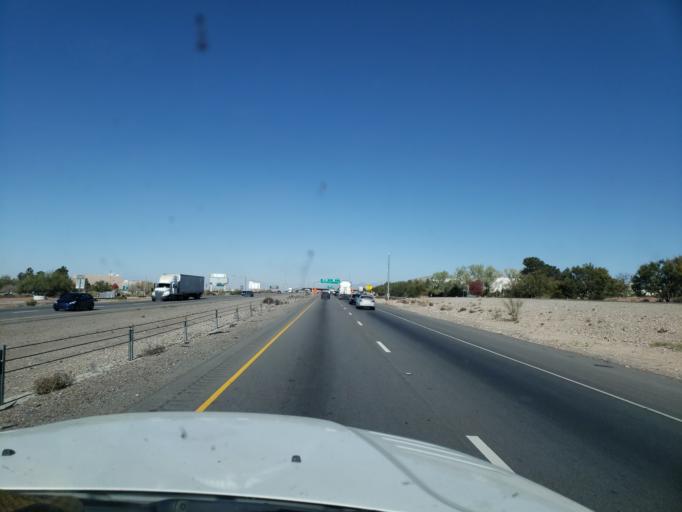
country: US
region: Texas
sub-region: El Paso County
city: Canutillo
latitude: 31.8962
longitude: -106.5827
